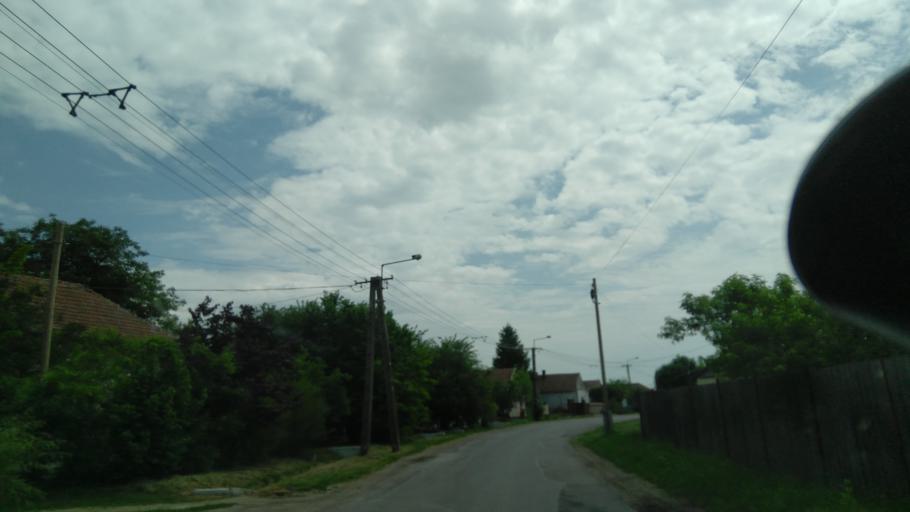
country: HU
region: Hajdu-Bihar
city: Komadi
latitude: 47.0175
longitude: 21.5988
